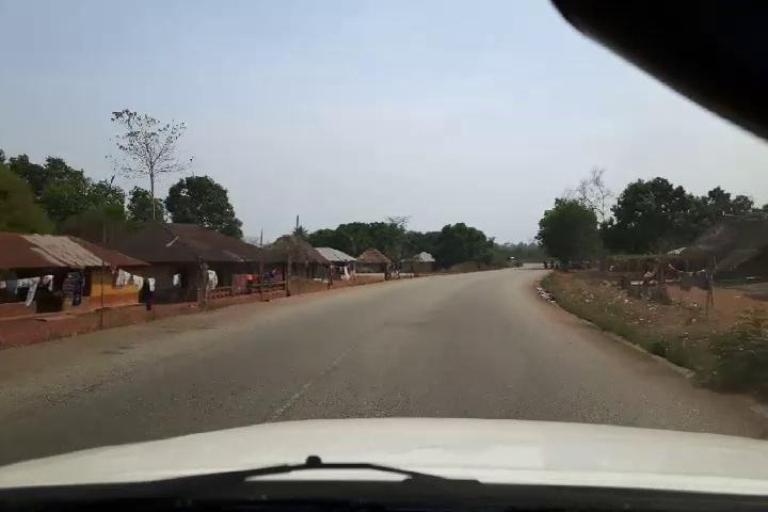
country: SL
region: Northern Province
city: Yonibana
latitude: 8.3980
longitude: -12.1945
